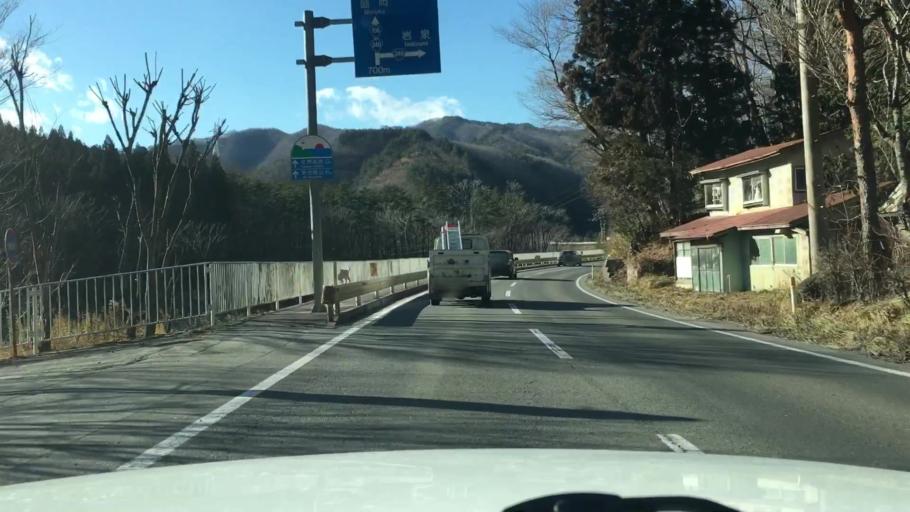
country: JP
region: Iwate
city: Miyako
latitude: 39.6193
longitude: 141.8076
